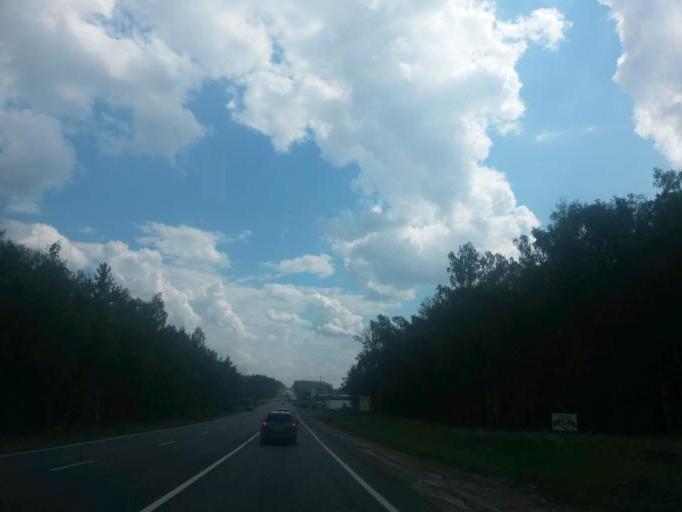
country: RU
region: Moskovskaya
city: Belyye Stolby
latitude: 55.3424
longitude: 37.7998
